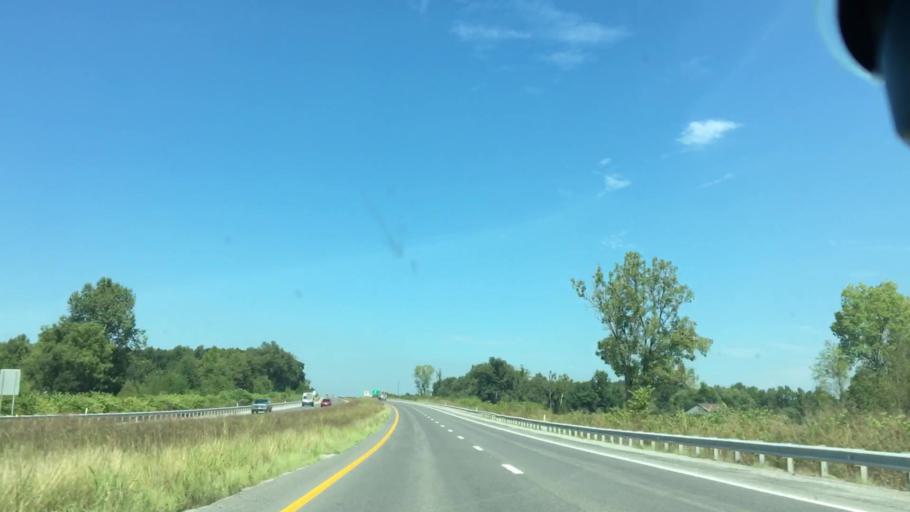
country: US
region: Kentucky
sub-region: Webster County
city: Sebree
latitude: 37.4784
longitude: -87.4760
